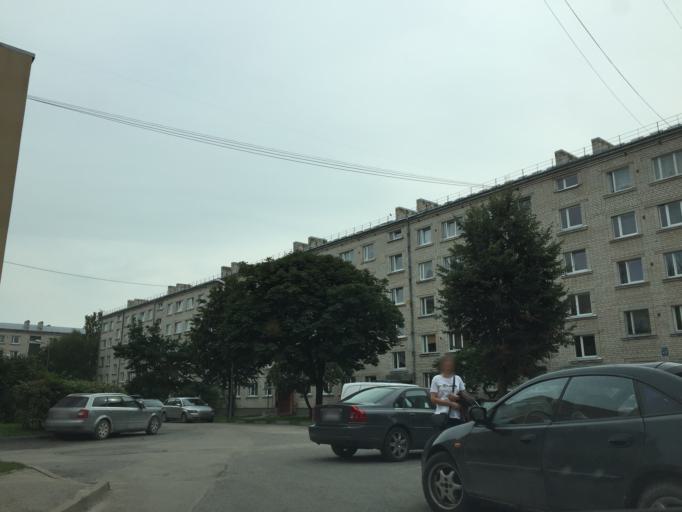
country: LV
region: Ogre
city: Ogre
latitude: 56.8242
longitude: 24.5957
